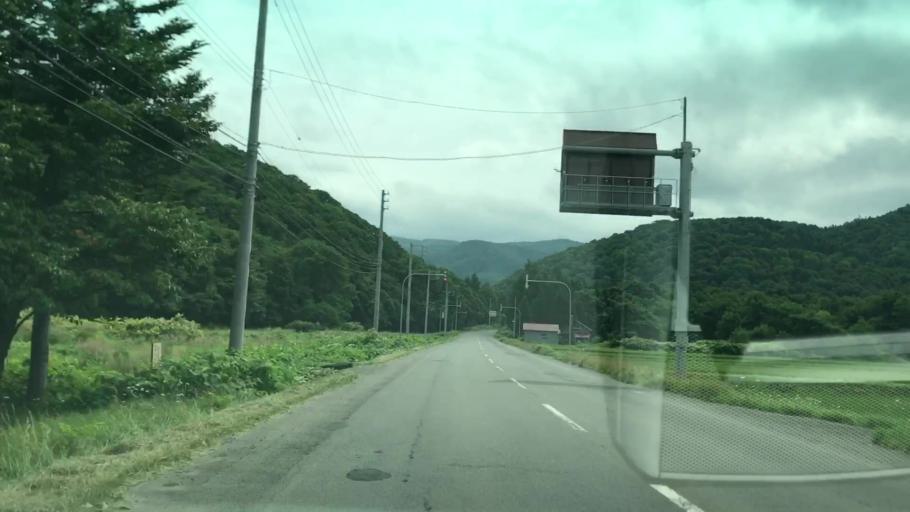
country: JP
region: Hokkaido
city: Yoichi
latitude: 43.0484
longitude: 140.8474
